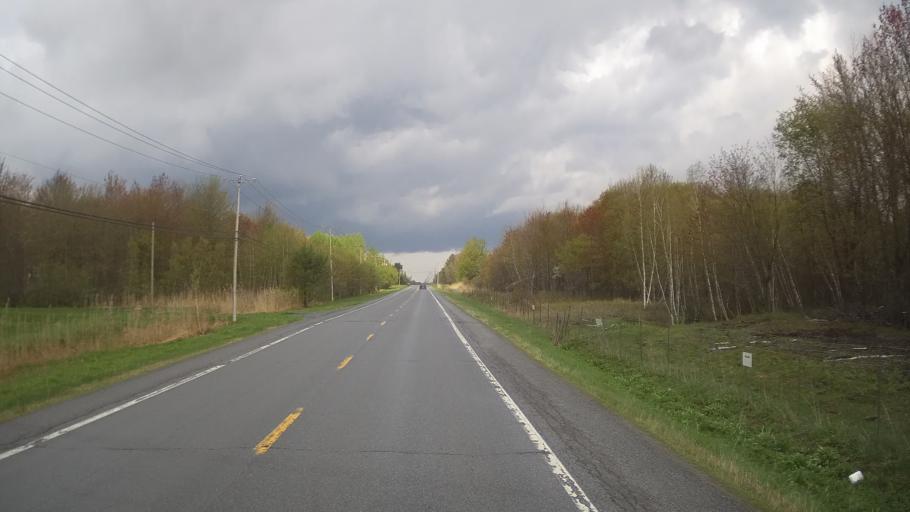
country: CA
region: Quebec
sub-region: Monteregie
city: Farnham
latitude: 45.3031
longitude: -73.0361
